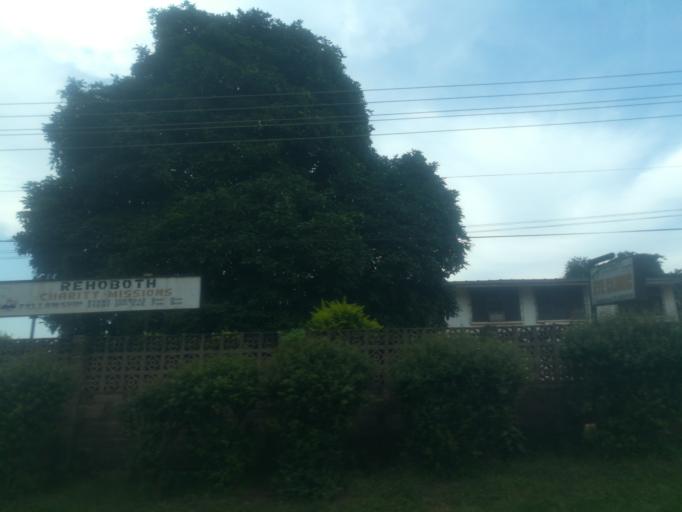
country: NG
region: Oyo
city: Ibadan
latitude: 7.4232
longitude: 3.9071
